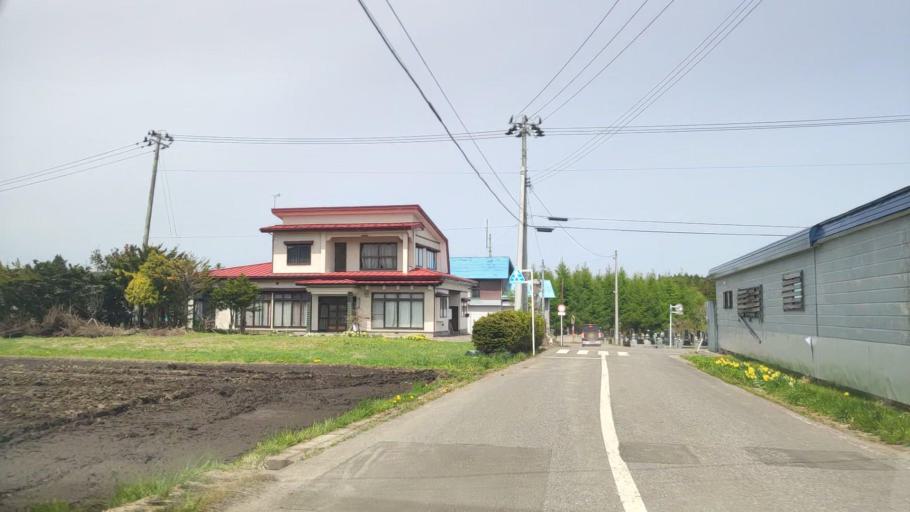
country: JP
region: Aomori
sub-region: Misawa Shi
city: Inuotose
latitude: 40.7780
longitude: 141.1224
